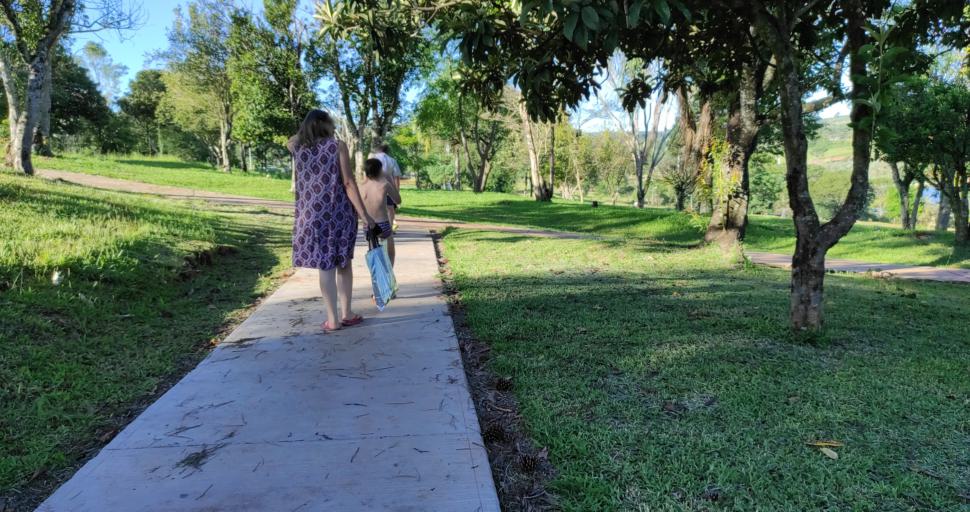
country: AR
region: Misiones
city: Dos de Mayo
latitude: -27.0429
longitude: -54.6830
